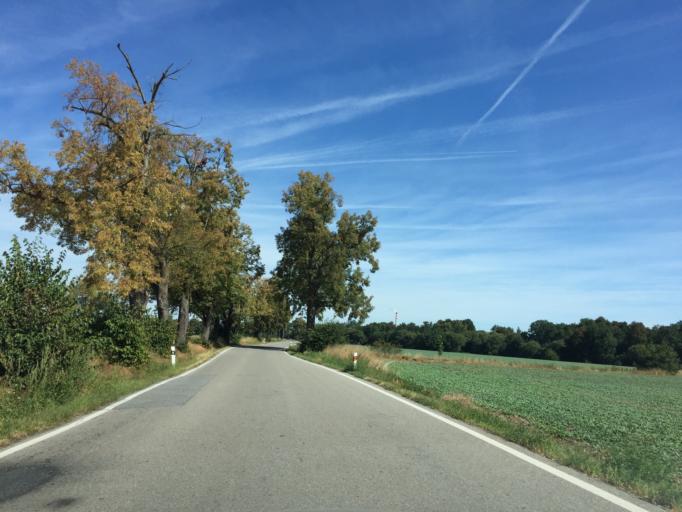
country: CZ
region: Jihocesky
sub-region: Okres Ceske Budejovice
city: Ceske Budejovice
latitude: 48.9480
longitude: 14.4825
